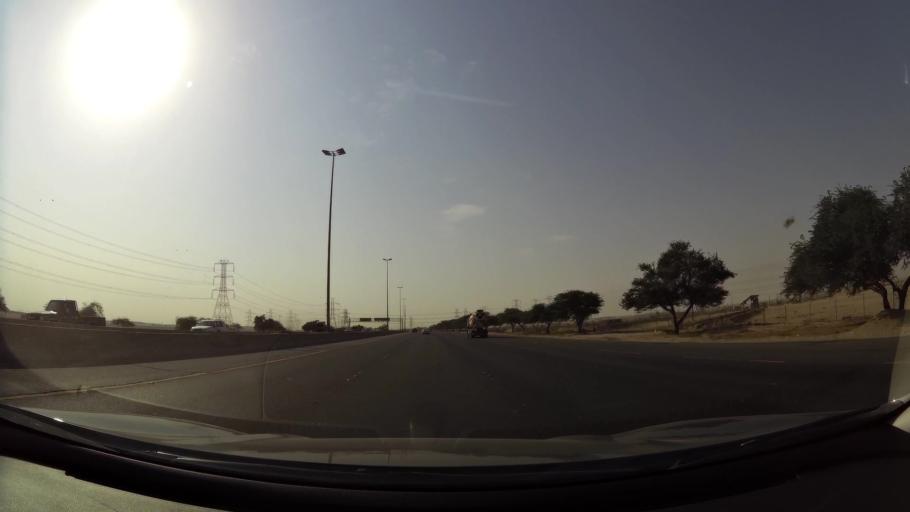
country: KW
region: Al Ahmadi
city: Al Ahmadi
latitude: 29.0200
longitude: 48.0915
